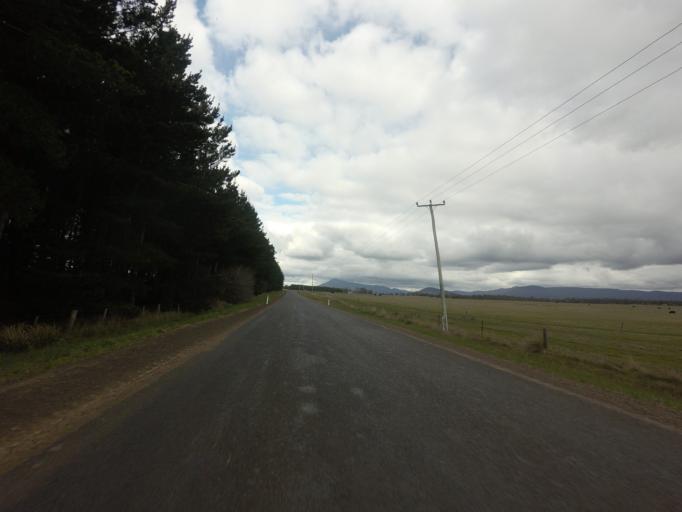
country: AU
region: Tasmania
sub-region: Northern Midlands
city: Longford
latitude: -41.7705
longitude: 147.0881
